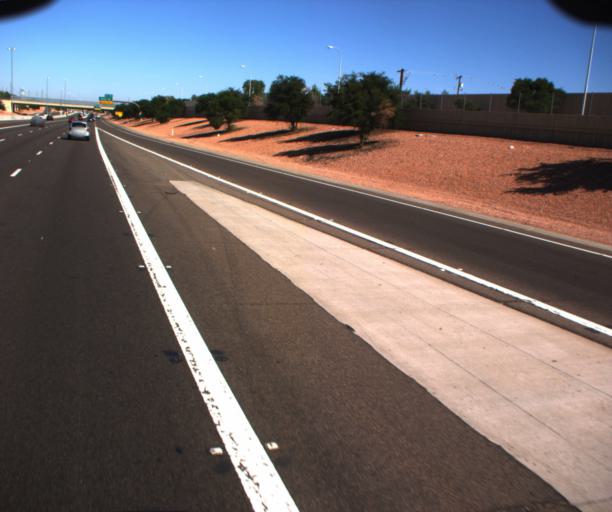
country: US
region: Arizona
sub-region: Maricopa County
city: San Carlos
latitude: 33.3394
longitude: -111.8930
